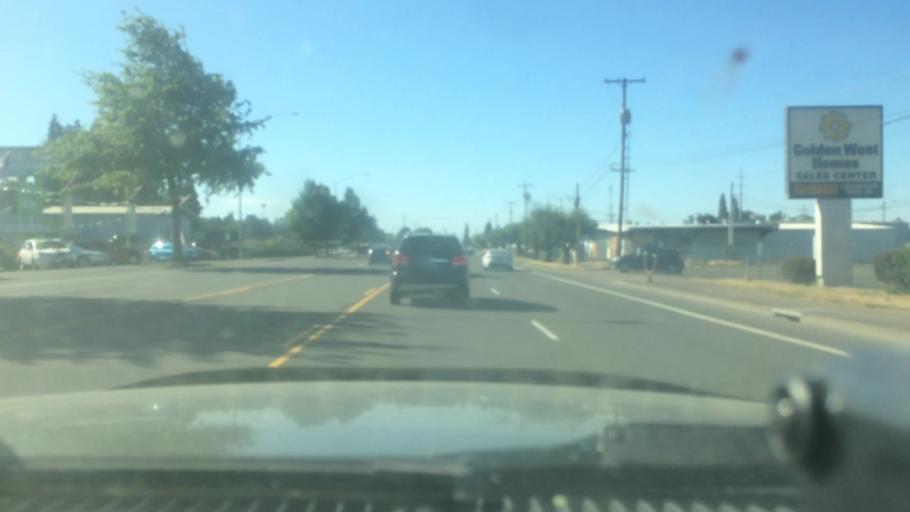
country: US
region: Oregon
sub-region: Lane County
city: Eugene
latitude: 44.0768
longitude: -123.1489
